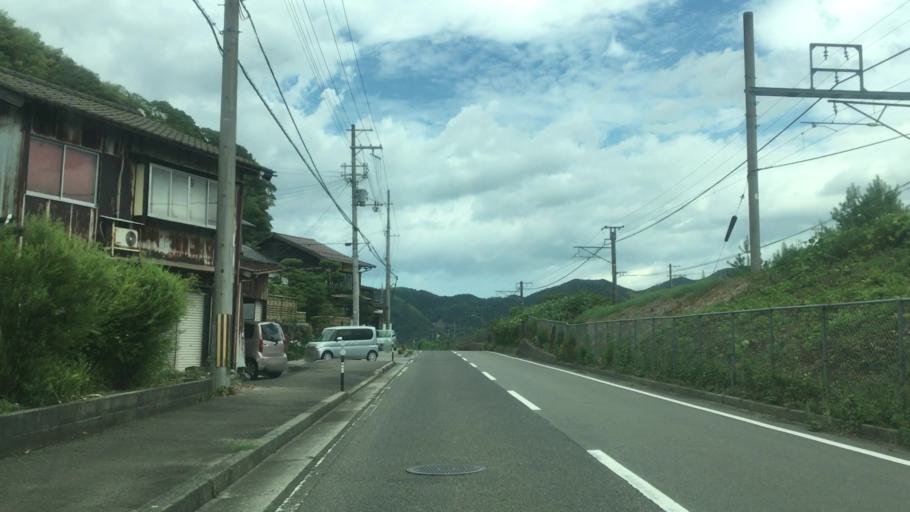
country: JP
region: Hyogo
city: Toyooka
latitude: 35.5666
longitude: 134.8036
